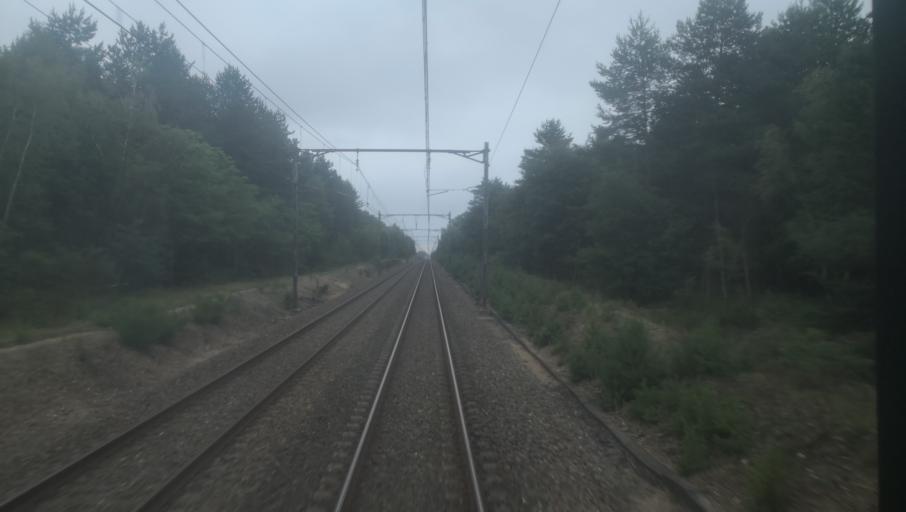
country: FR
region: Centre
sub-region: Departement du Loir-et-Cher
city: Theillay
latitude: 47.3525
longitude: 2.0473
